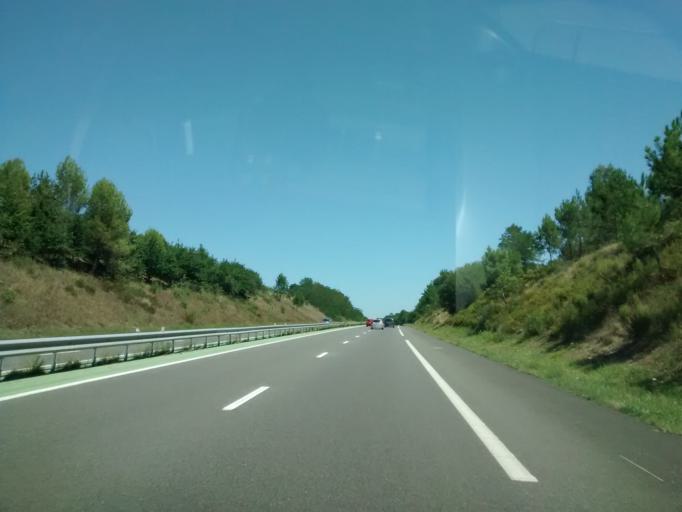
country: FR
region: Aquitaine
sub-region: Departement de la Dordogne
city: Montpon-Menesterol
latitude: 44.9927
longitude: 0.2149
